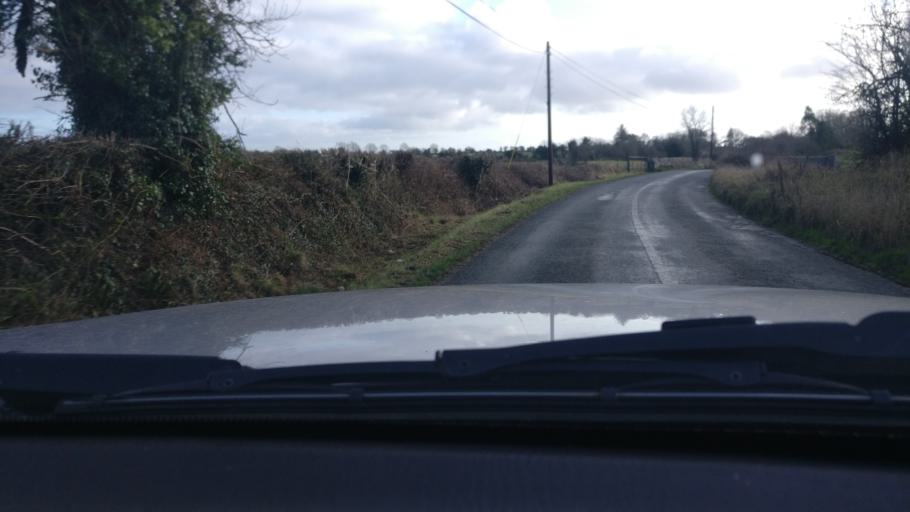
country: IE
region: Connaught
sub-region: County Galway
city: Ballinasloe
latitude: 53.2268
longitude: -8.2932
